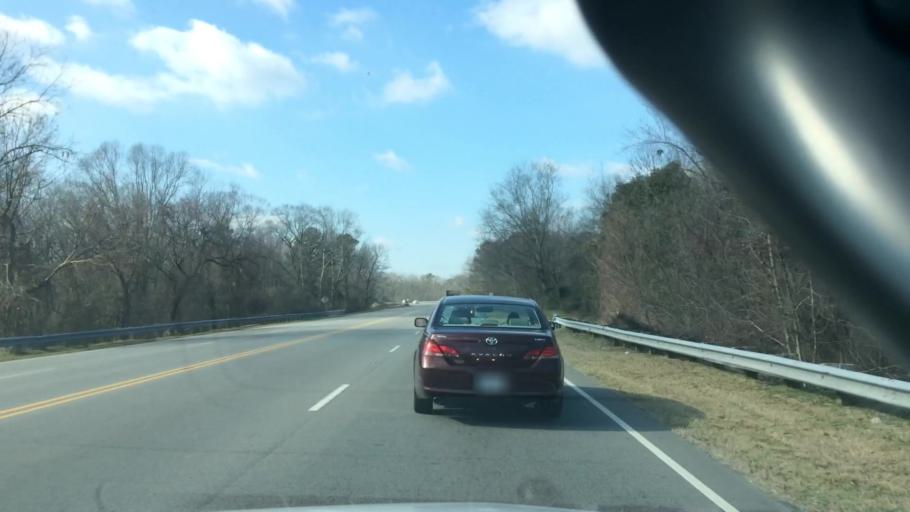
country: US
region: North Carolina
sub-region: Lenoir County
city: Kinston
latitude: 35.2590
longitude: -77.5876
